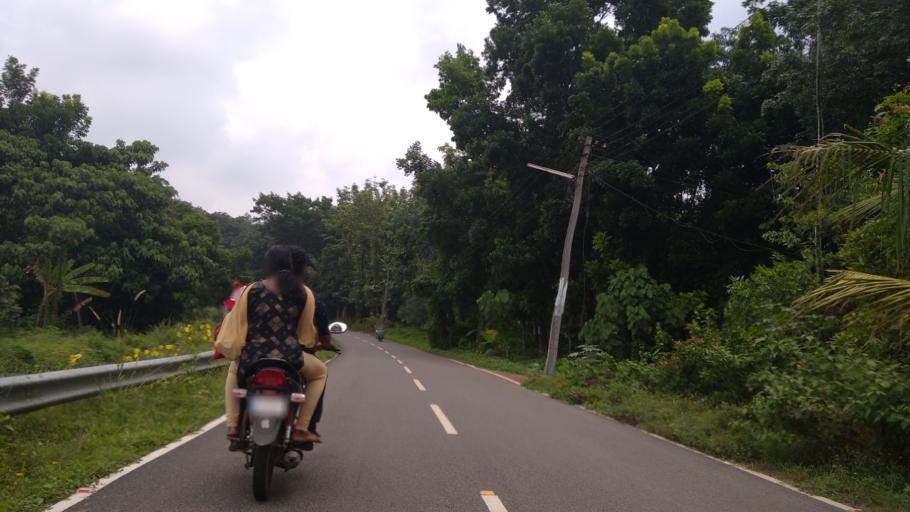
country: IN
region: Kerala
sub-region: Ernakulam
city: Perumbavoor
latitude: 10.0210
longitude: 76.4862
